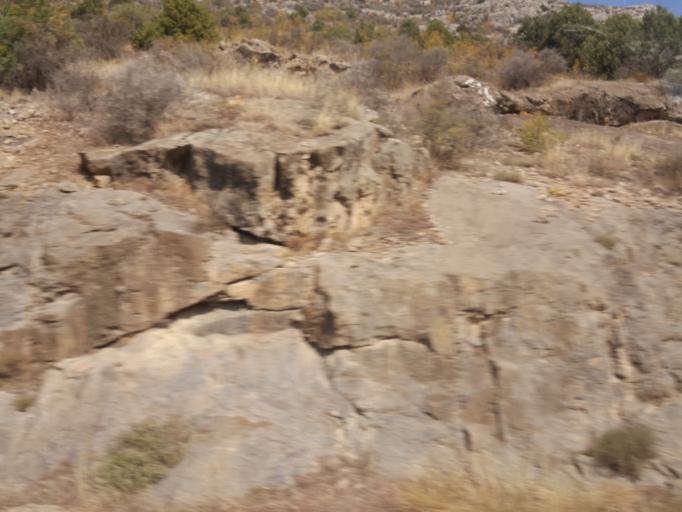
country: TR
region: Yozgat
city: Cekerek
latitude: 40.1199
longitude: 35.6124
